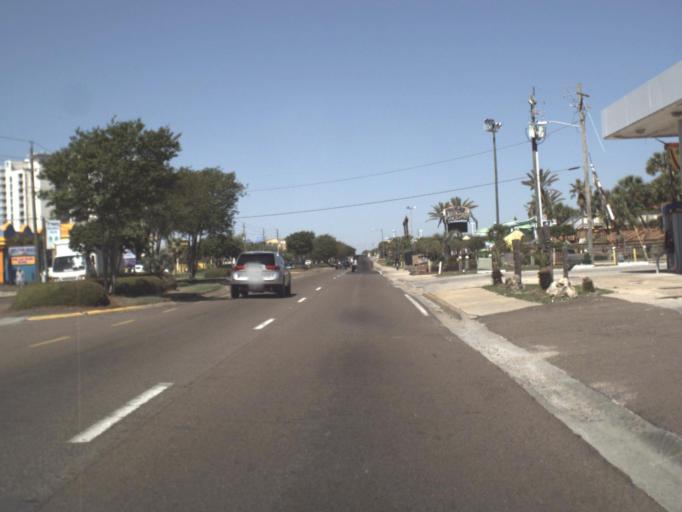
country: US
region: Florida
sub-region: Okaloosa County
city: Destin
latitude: 30.3871
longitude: -86.4715
